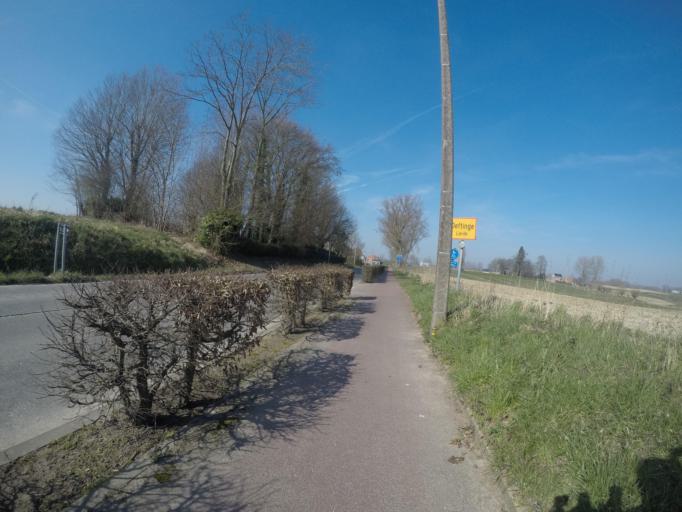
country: BE
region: Flanders
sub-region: Provincie Oost-Vlaanderen
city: Geraardsbergen
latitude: 50.7808
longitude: 3.8550
